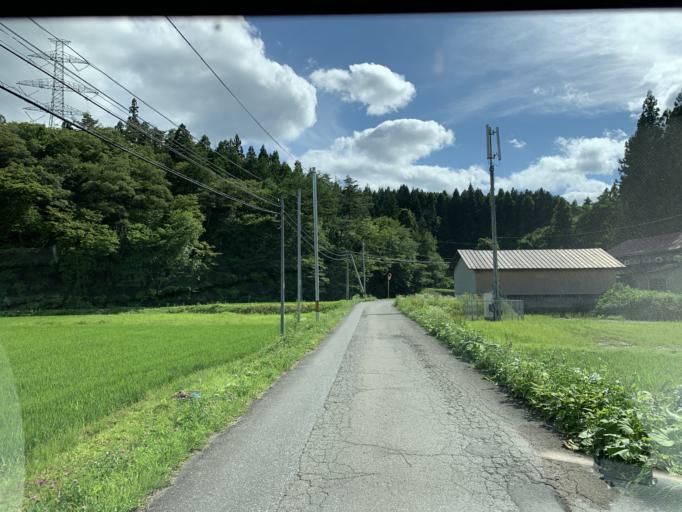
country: JP
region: Iwate
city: Ichinoseki
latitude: 38.9350
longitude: 141.0095
